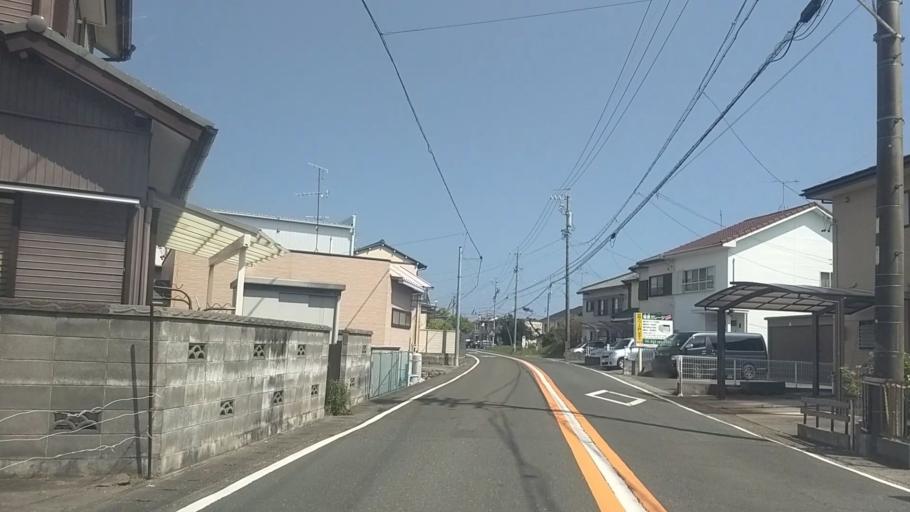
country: JP
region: Shizuoka
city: Hamamatsu
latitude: 34.6849
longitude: 137.6727
